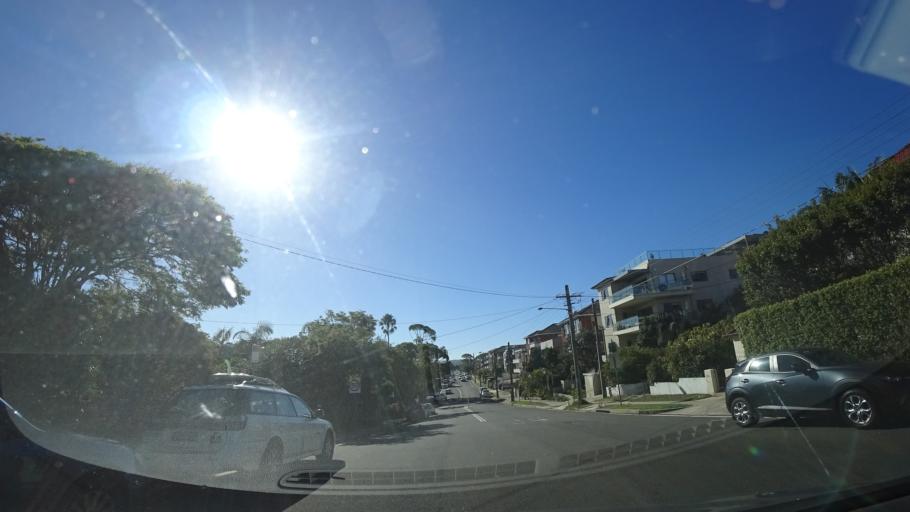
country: AU
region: New South Wales
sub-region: Warringah
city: Freshwater
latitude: -33.7836
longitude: 151.2864
